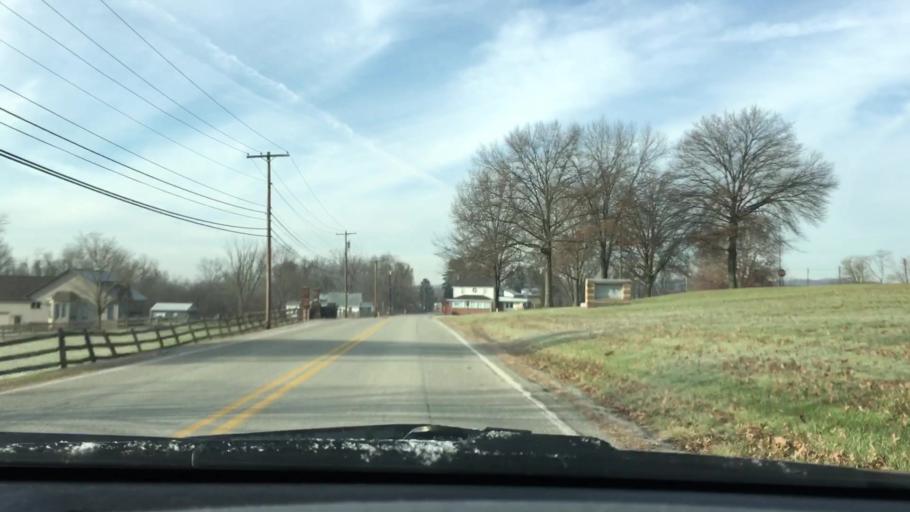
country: US
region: Pennsylvania
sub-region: Westmoreland County
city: Collinsburg
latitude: 40.2588
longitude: -79.7330
